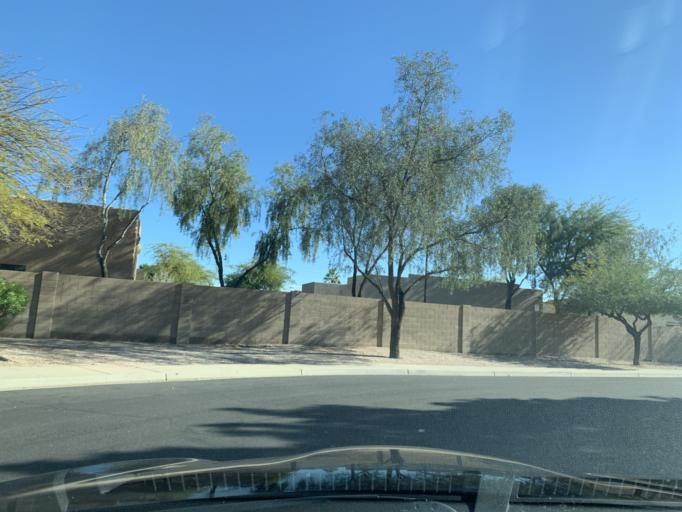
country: US
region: Arizona
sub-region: Pinal County
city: Apache Junction
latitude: 33.3858
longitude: -111.6179
